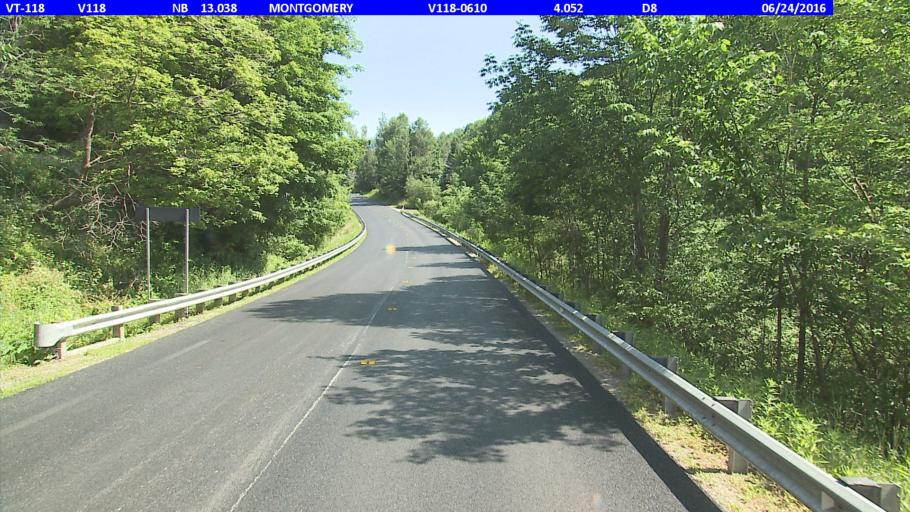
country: US
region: Vermont
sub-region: Franklin County
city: Richford
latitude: 44.8560
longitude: -72.6103
